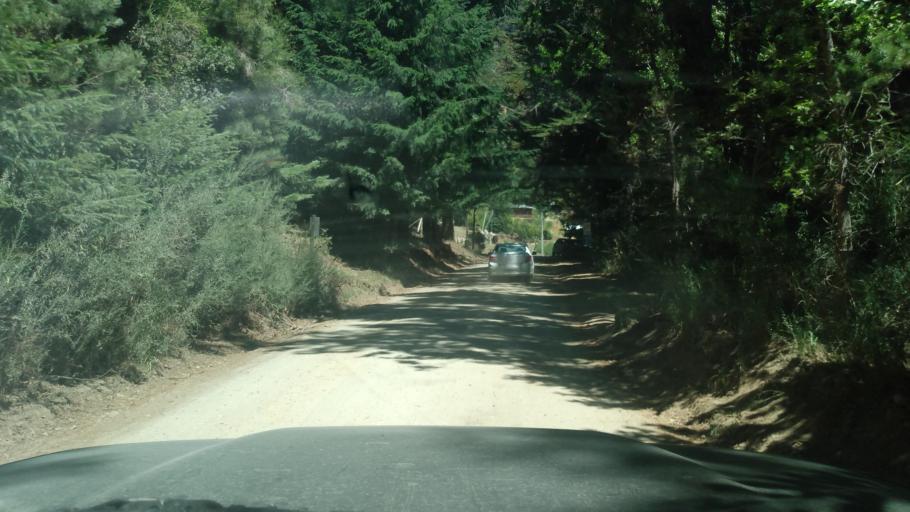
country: AR
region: Rio Negro
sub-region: Departamento de Bariloche
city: San Carlos de Bariloche
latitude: -41.1009
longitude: -71.4944
